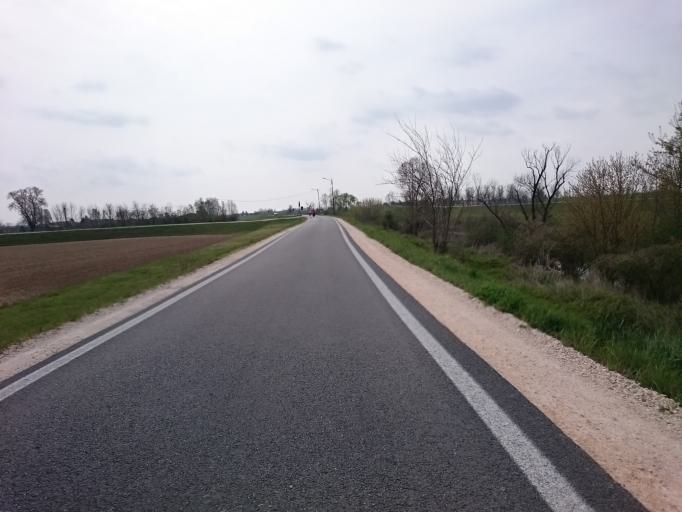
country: IT
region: Veneto
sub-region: Provincia di Padova
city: Polverara
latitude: 45.3312
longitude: 11.9388
